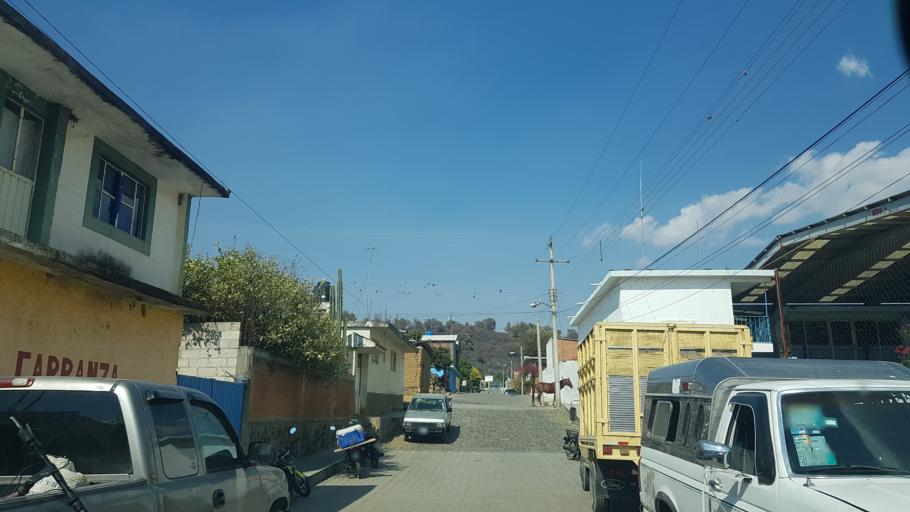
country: MX
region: Puebla
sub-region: Atlixco
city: Colonia Agricola de Ocotepec (Colonia San Jose)
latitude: 18.9271
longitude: -98.5437
